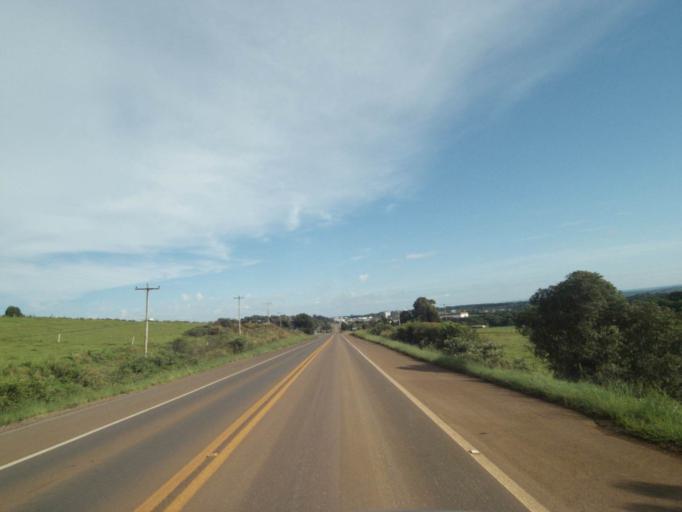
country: BR
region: Rio Grande do Sul
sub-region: Lagoa Vermelha
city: Lagoa Vermelha
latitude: -28.2285
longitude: -51.5061
